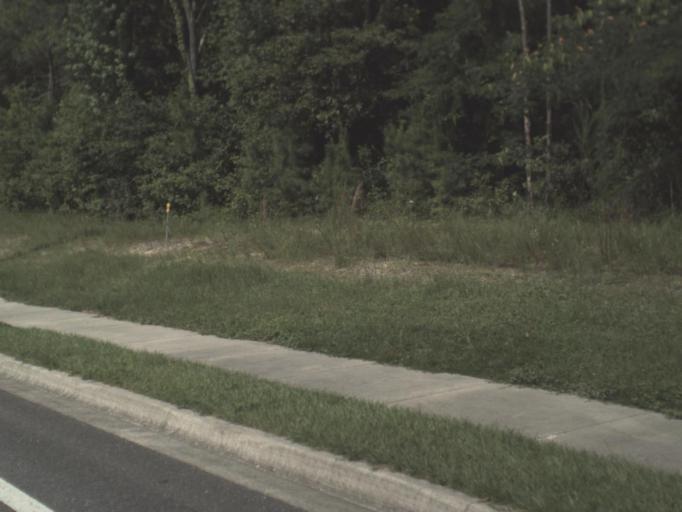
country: US
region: Florida
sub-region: Columbia County
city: Lake City
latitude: 30.1242
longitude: -82.6532
